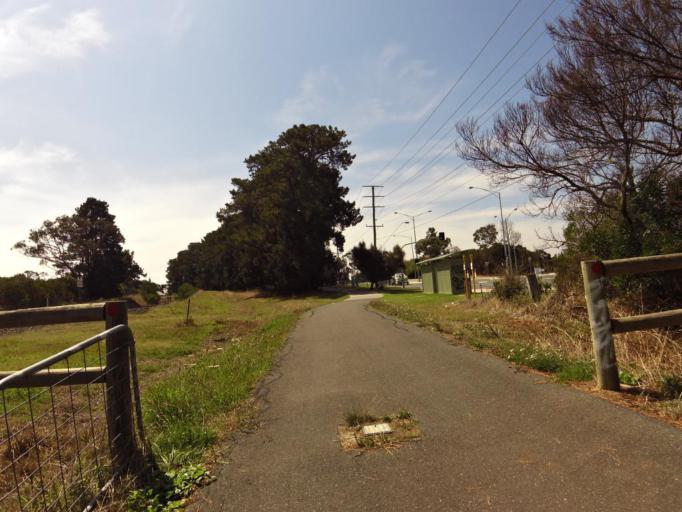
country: AU
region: Victoria
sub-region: Mornington Peninsula
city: Tyabb
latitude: -38.2653
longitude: 145.1895
